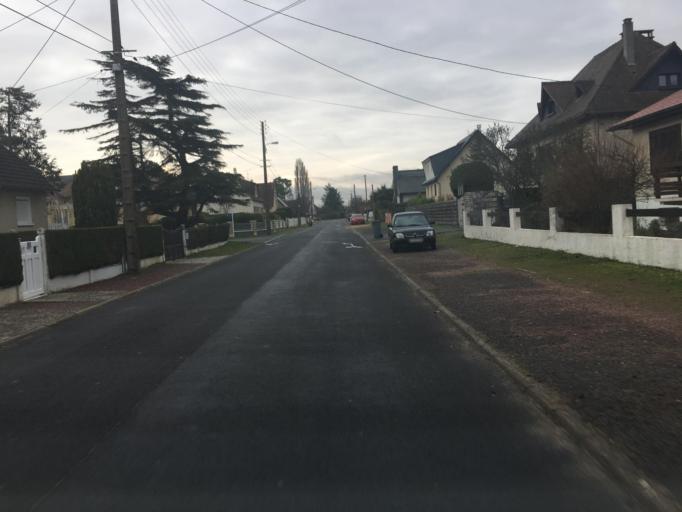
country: FR
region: Lower Normandy
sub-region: Departement du Calvados
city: Merville-Franceville-Plage
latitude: 49.2804
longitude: -0.2076
